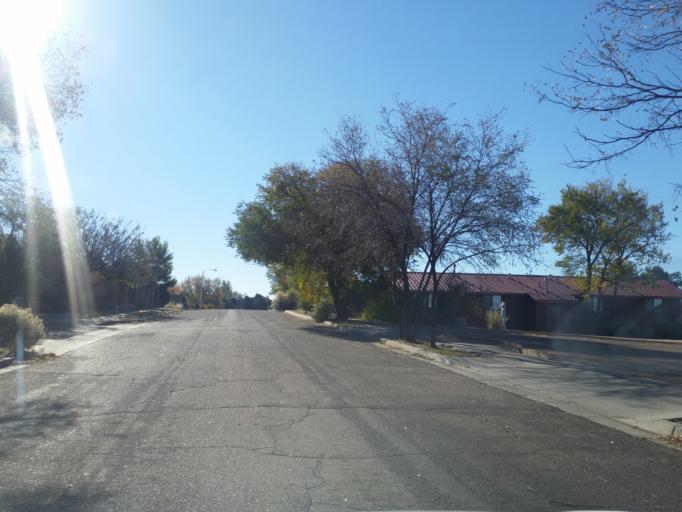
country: US
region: New Mexico
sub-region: Santa Fe County
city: Santa Fe
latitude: 35.6491
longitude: -105.9325
